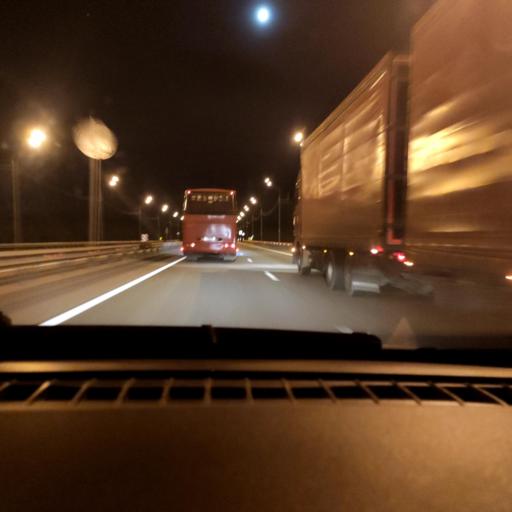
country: RU
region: Lipetsk
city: Khlevnoye
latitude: 52.2357
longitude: 39.0791
